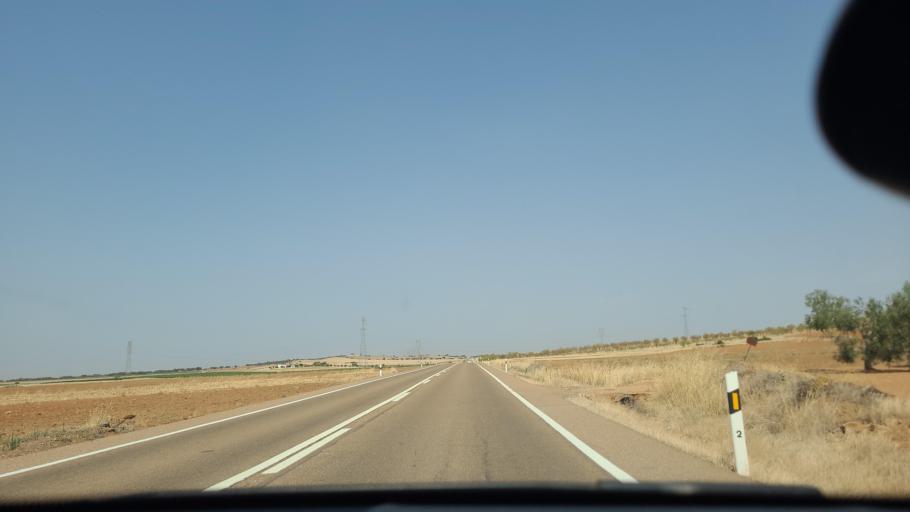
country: ES
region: Extremadura
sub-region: Provincia de Badajoz
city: Usagre
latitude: 38.3538
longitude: -6.2006
